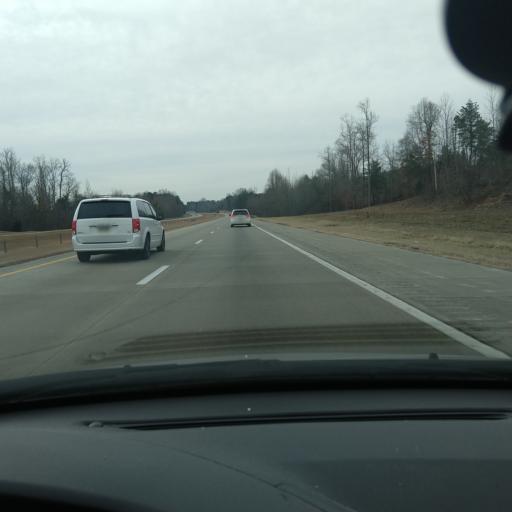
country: US
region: North Carolina
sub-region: Davidson County
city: Welcome
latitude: 35.9147
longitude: -80.2340
